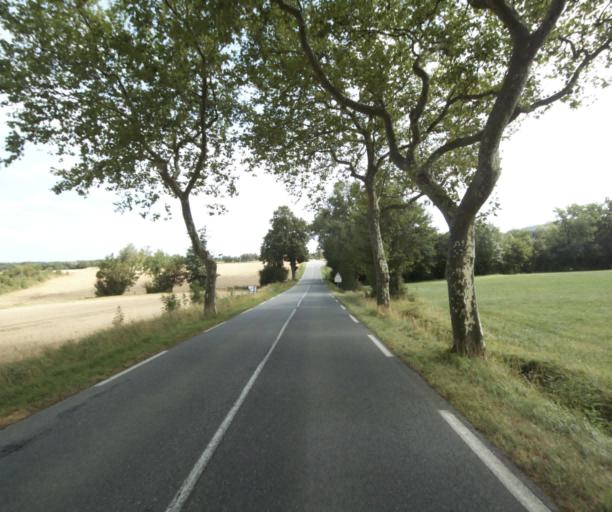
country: FR
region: Midi-Pyrenees
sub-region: Departement du Tarn
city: Soreze
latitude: 43.4692
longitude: 2.0998
